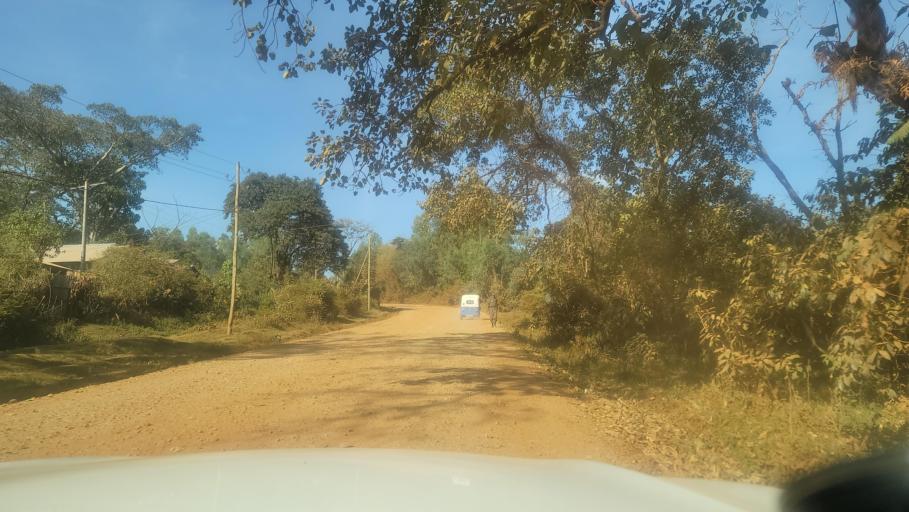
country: ET
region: Oromiya
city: Agaro
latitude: 7.8401
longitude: 36.5488
